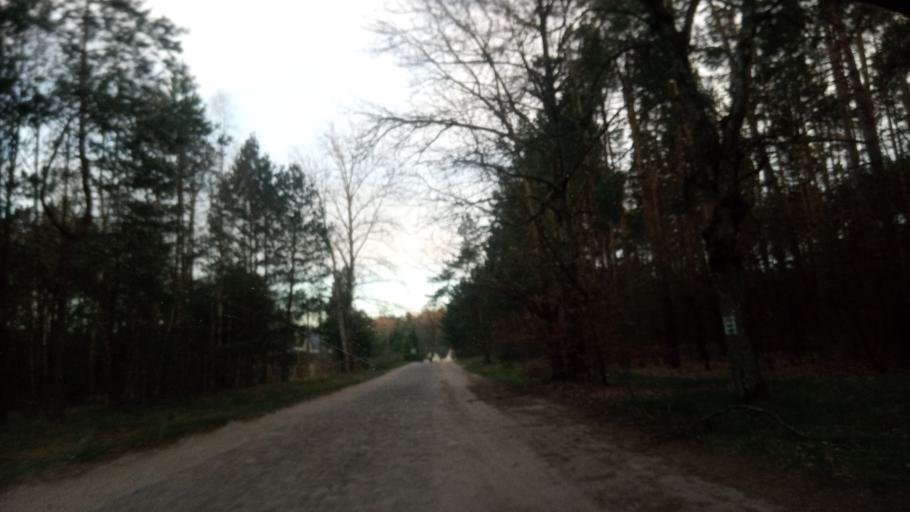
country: PL
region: West Pomeranian Voivodeship
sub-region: Powiat szczecinecki
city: Lubowo
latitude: 53.5546
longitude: 16.3894
